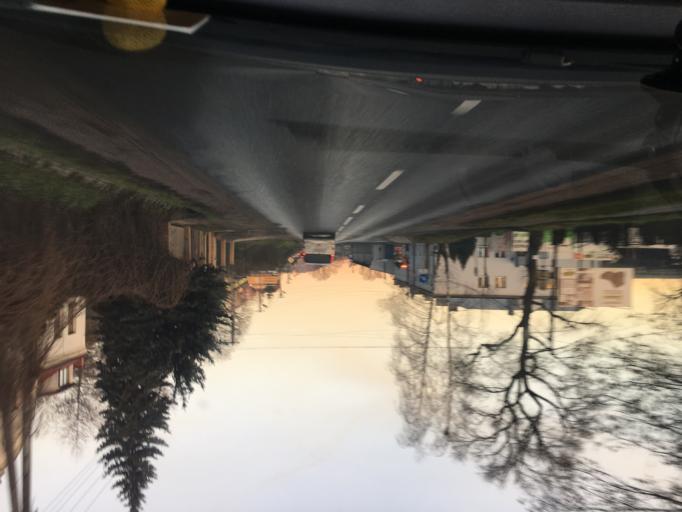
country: PL
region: Lesser Poland Voivodeship
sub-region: Krakow
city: Krakow
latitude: 50.0477
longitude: 19.8910
